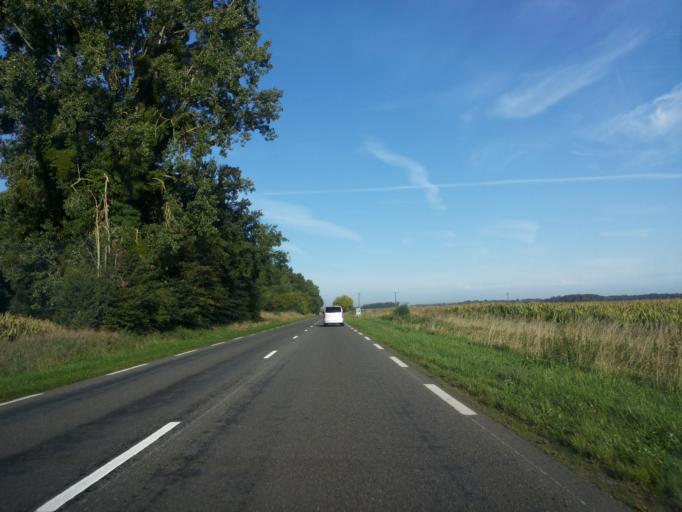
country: FR
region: Picardie
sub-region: Departement de l'Aisne
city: Athies-sous-Laon
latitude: 49.5472
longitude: 3.7266
